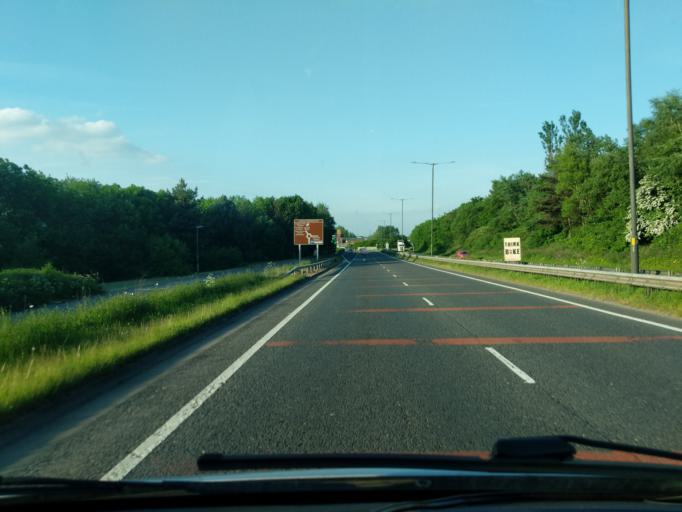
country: GB
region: England
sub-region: St. Helens
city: St Helens
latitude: 53.4398
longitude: -2.7333
